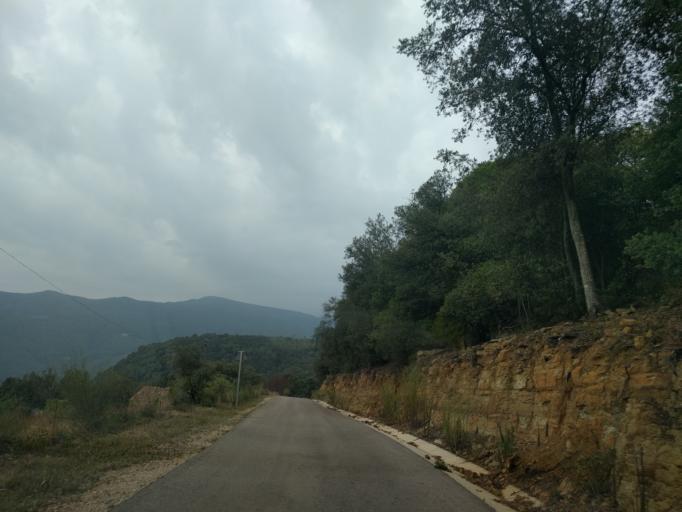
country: ES
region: Catalonia
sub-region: Provincia de Girona
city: la Cellera de Ter
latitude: 42.0258
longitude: 2.6254
